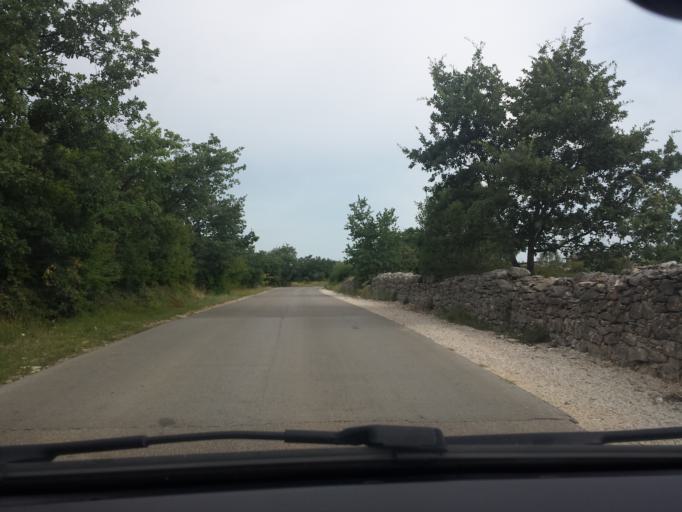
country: HR
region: Istarska
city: Galizana
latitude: 44.9426
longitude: 13.8655
